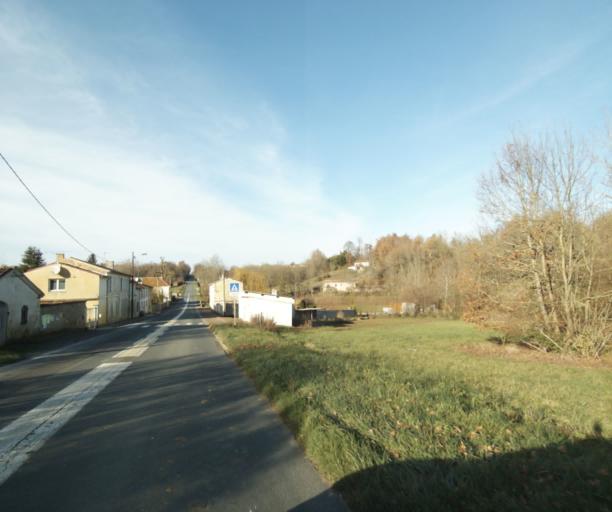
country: FR
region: Poitou-Charentes
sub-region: Departement de la Charente-Maritime
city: Burie
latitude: 45.7943
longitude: -0.4404
